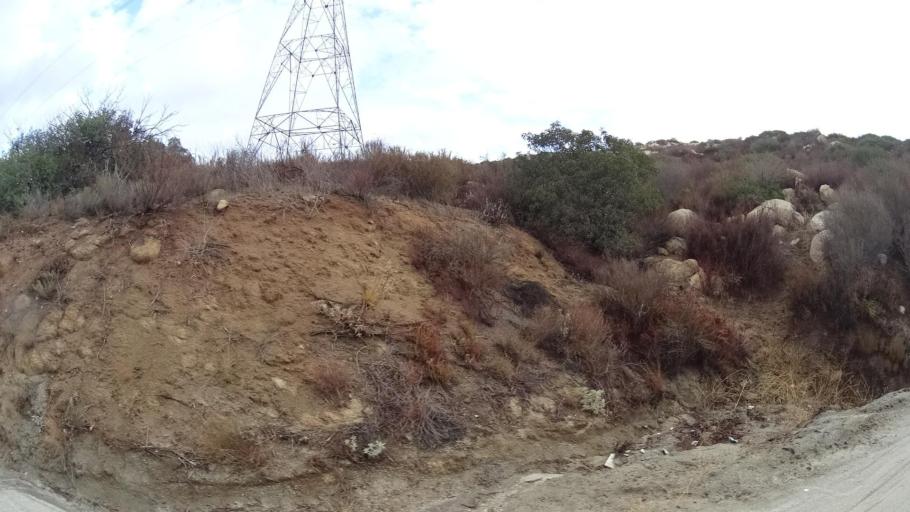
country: MX
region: Baja California
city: Tecate
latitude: 32.5959
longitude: -116.6352
